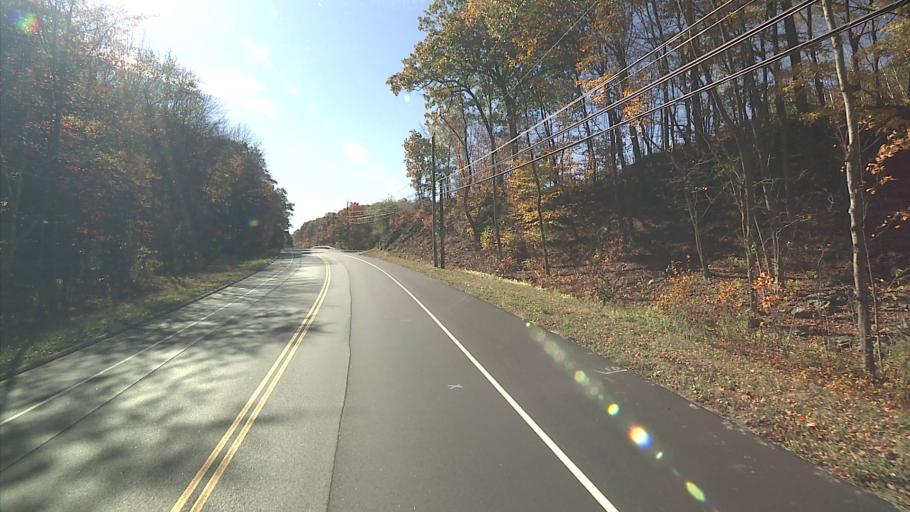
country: US
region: Connecticut
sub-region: Litchfield County
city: Watertown
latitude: 41.6322
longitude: -73.1018
